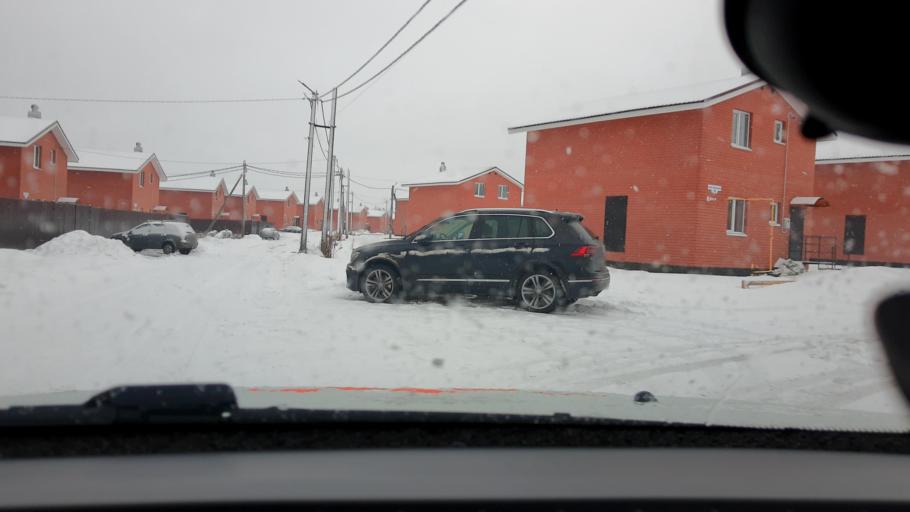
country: RU
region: Nizjnij Novgorod
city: Afonino
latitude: 56.1975
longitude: 44.0715
